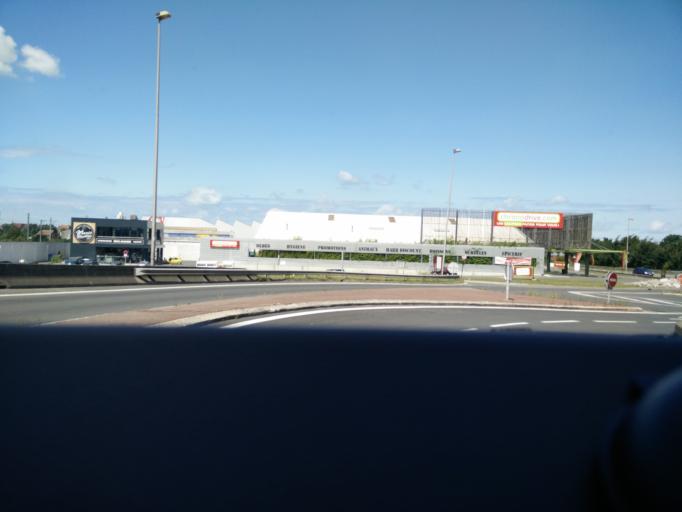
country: FR
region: Nord-Pas-de-Calais
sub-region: Departement du Nord
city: Coudekerque-Branche
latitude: 51.0142
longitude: 2.3775
